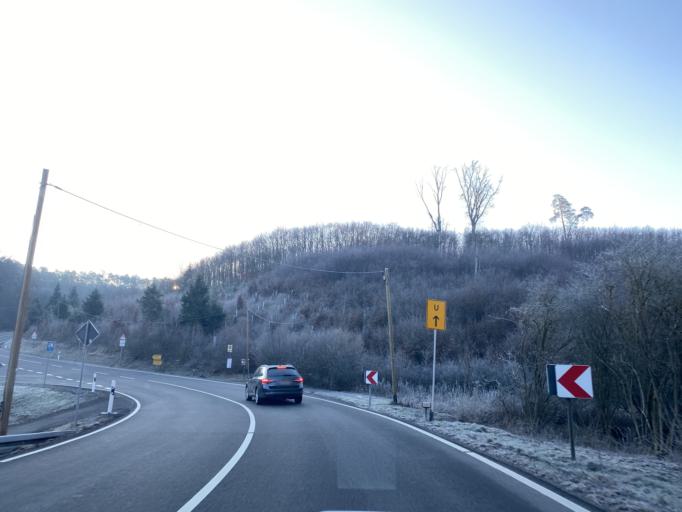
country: DE
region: Baden-Wuerttemberg
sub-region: Regierungsbezirk Stuttgart
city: Weissach
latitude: 48.8474
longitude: 8.9612
